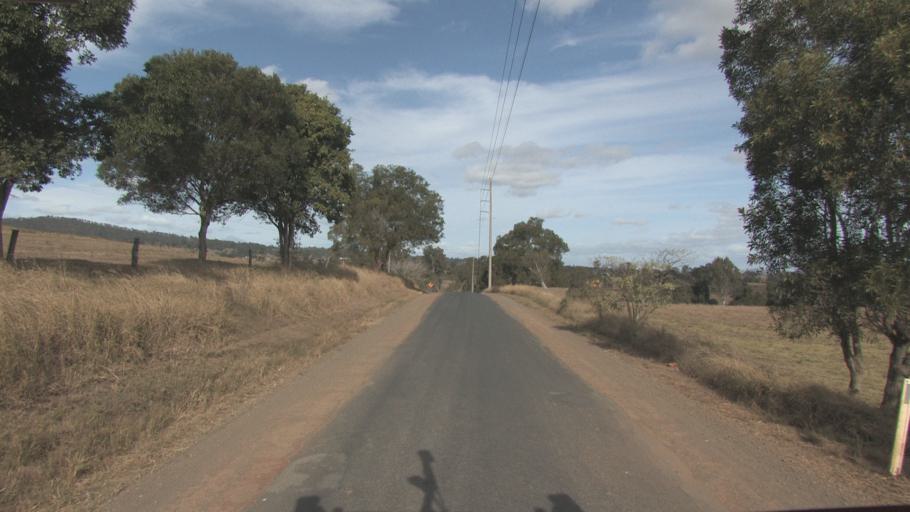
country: AU
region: Queensland
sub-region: Logan
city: Cedar Vale
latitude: -27.9100
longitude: 153.0134
